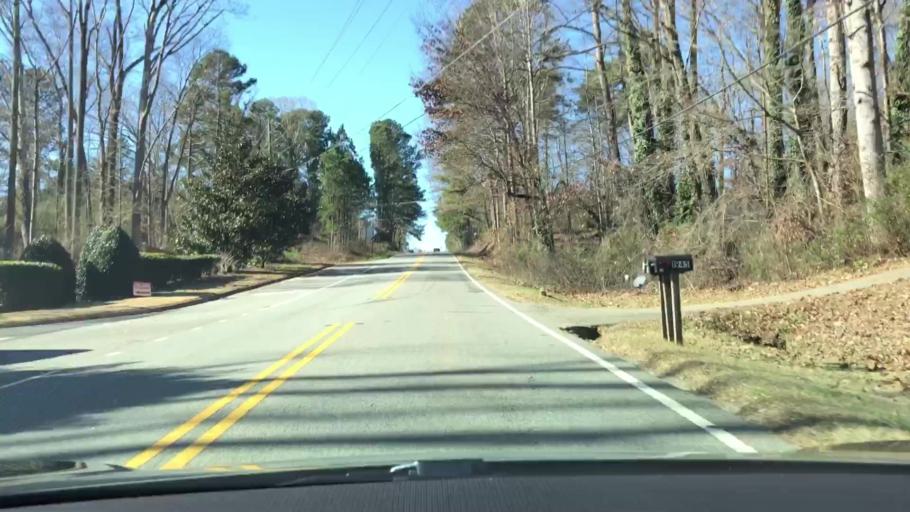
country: US
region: Georgia
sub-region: Forsyth County
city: Cumming
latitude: 34.1834
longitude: -84.1015
